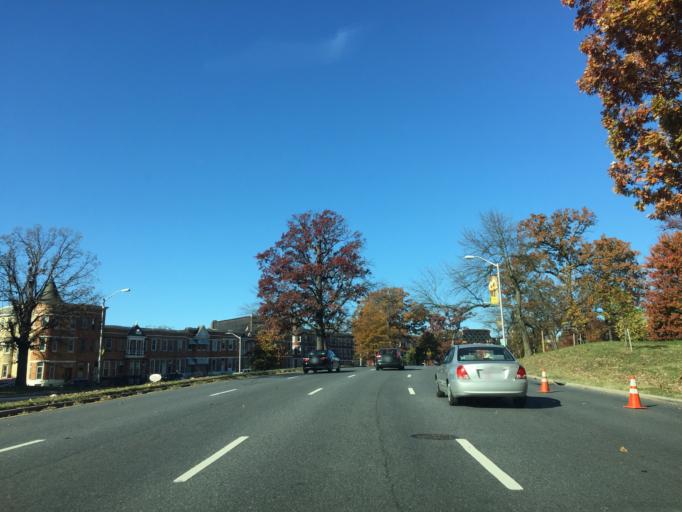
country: US
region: Maryland
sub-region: City of Baltimore
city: Baltimore
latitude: 39.3166
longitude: -76.6448
